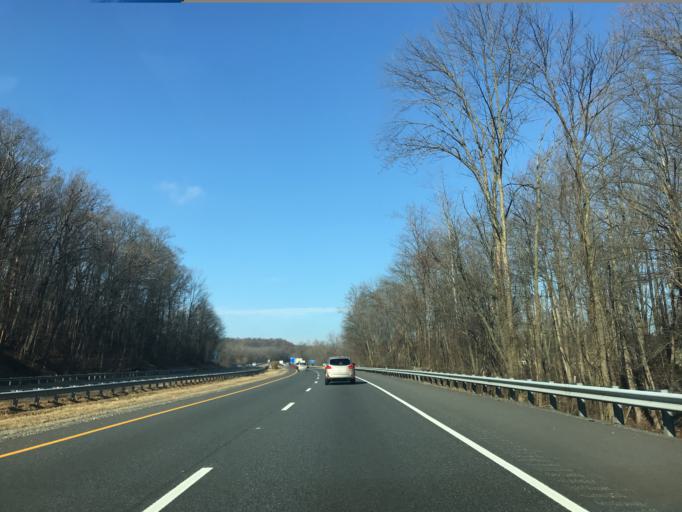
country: US
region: Maryland
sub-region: Baltimore County
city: Hunt Valley
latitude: 39.5650
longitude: -76.6664
